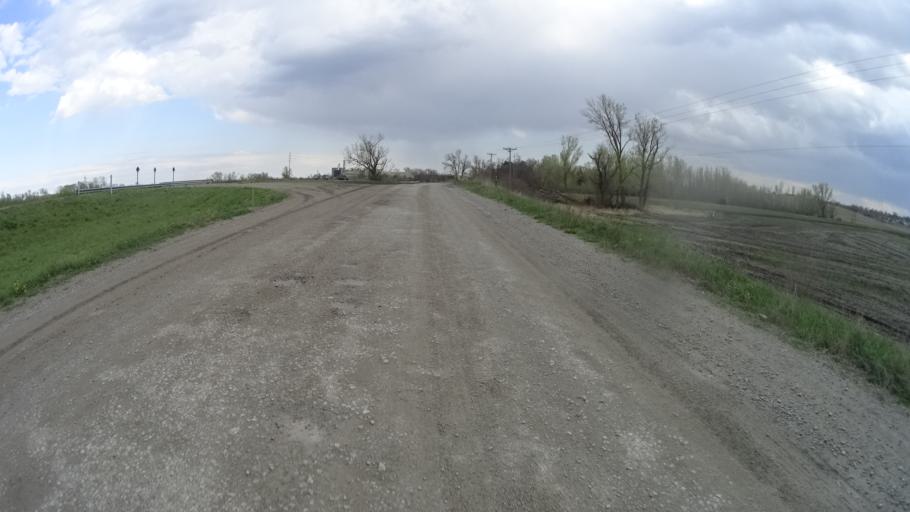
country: US
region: Nebraska
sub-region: Sarpy County
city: Offutt Air Force Base
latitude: 41.1018
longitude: -95.9166
